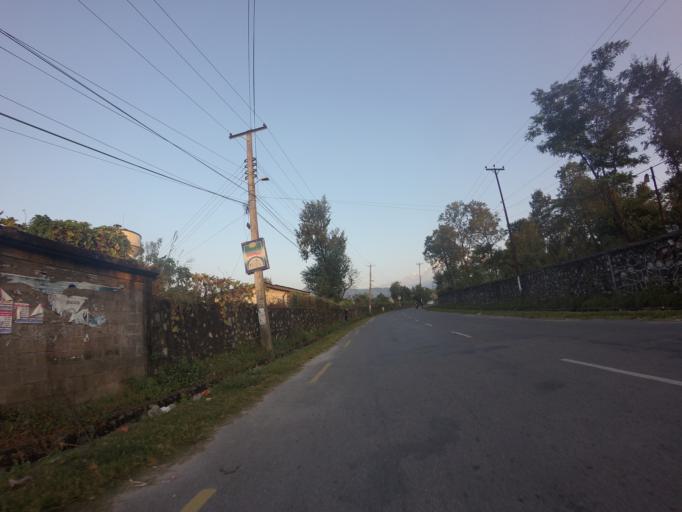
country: NP
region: Western Region
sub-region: Gandaki Zone
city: Pokhara
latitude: 28.2134
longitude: 83.9987
